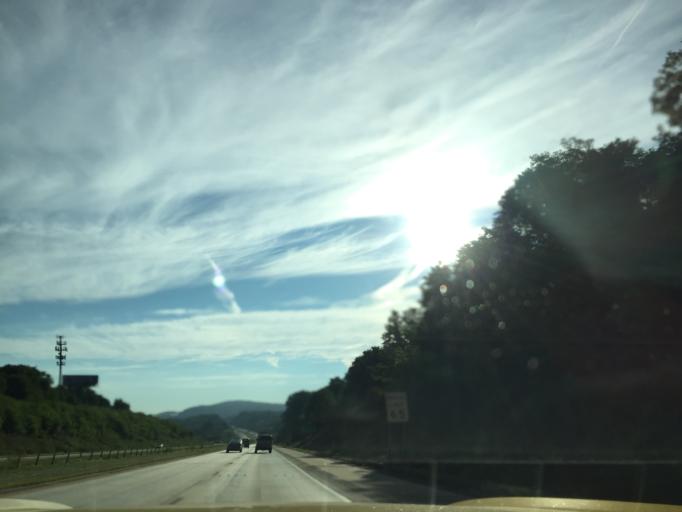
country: US
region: Pennsylvania
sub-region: Northampton County
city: Old Orchard
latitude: 40.6420
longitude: -75.2654
